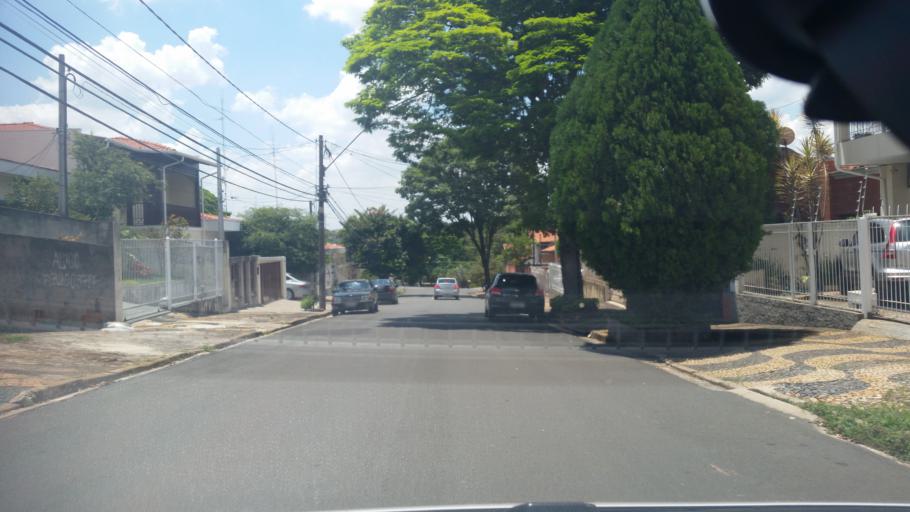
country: BR
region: Sao Paulo
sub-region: Campinas
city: Campinas
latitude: -22.8775
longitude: -47.0505
